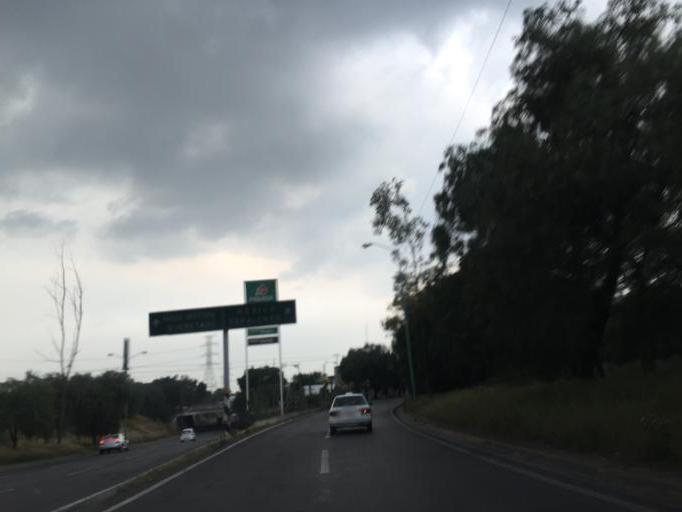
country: MX
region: Mexico
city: Cuautitlan Izcalli
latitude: 19.6545
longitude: -99.1995
